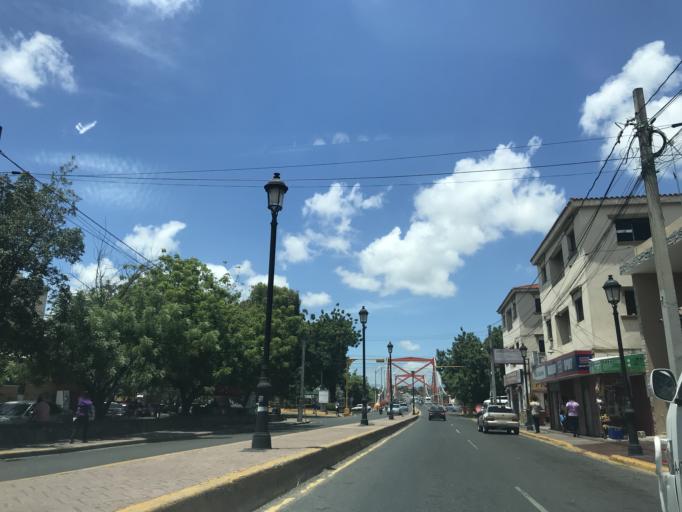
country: DO
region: Santiago
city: Santiago de los Caballeros
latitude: 19.4505
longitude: -70.7079
